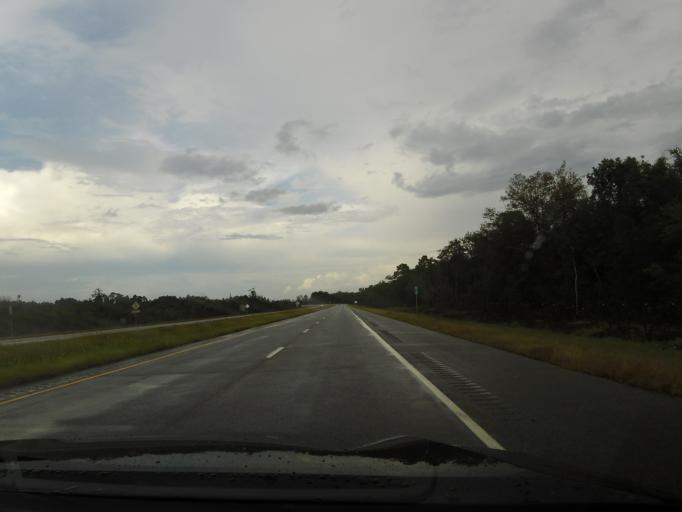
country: US
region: Georgia
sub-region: Wayne County
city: Jesup
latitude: 31.6014
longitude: -81.8644
